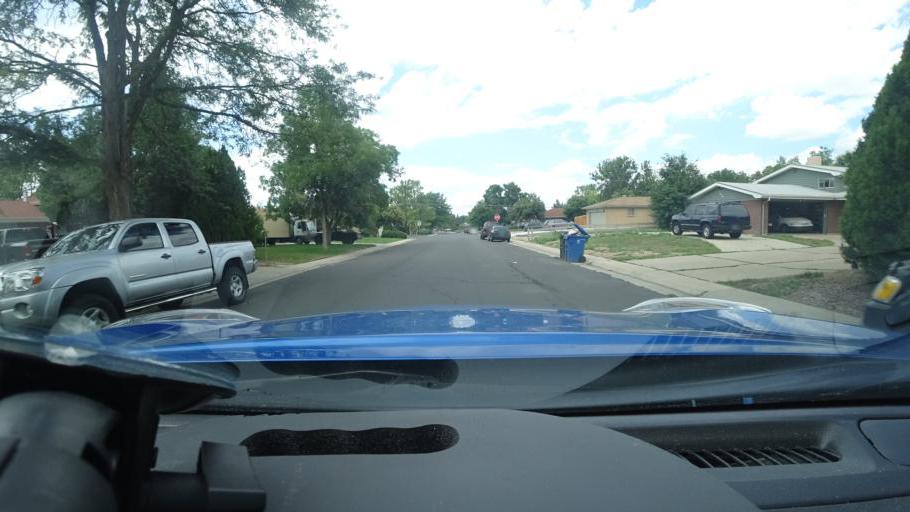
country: US
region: Colorado
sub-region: Adams County
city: Aurora
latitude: 39.7214
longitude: -104.8364
